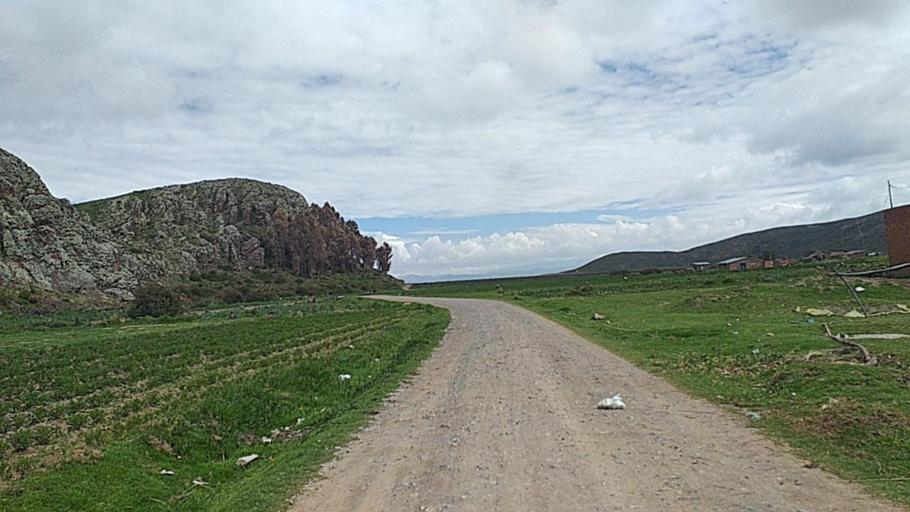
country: BO
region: La Paz
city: Batallas
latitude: -16.3474
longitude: -68.6347
